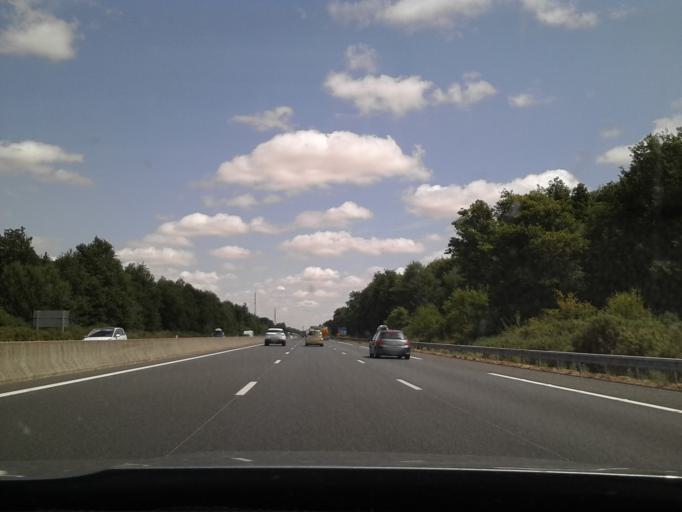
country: FR
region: Centre
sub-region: Departement d'Indre-et-Loire
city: Auzouer-en-Touraine
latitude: 47.5311
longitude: 0.9526
